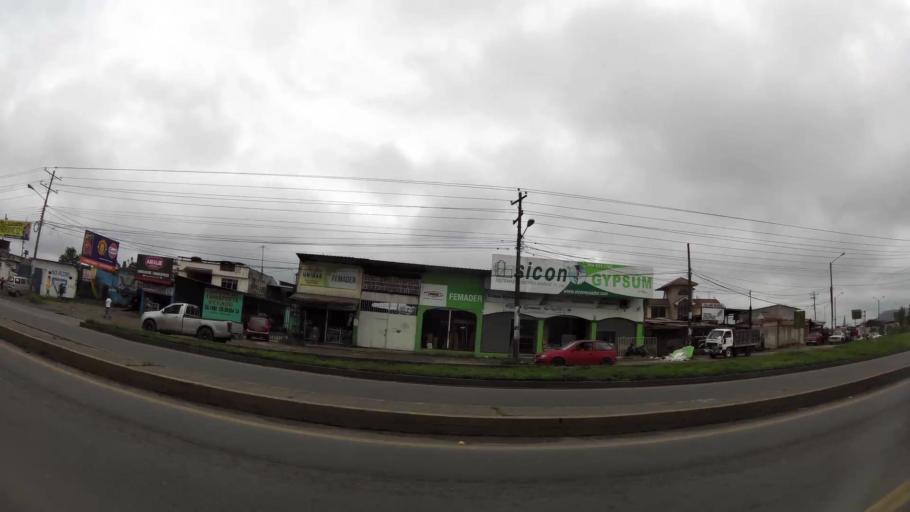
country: EC
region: Santo Domingo de los Tsachilas
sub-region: Canton Santo Domingo de los Colorados
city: Santo Domingo de los Colorados
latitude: -0.2736
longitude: -79.1995
